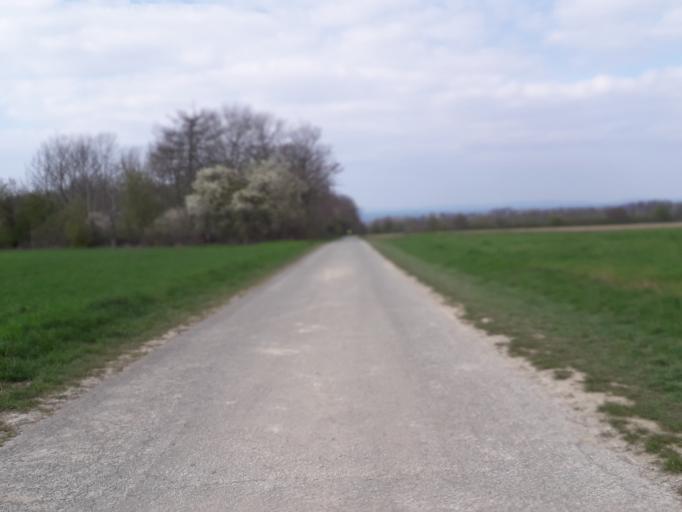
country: DE
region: North Rhine-Westphalia
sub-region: Regierungsbezirk Detmold
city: Paderborn
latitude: 51.6906
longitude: 8.7646
